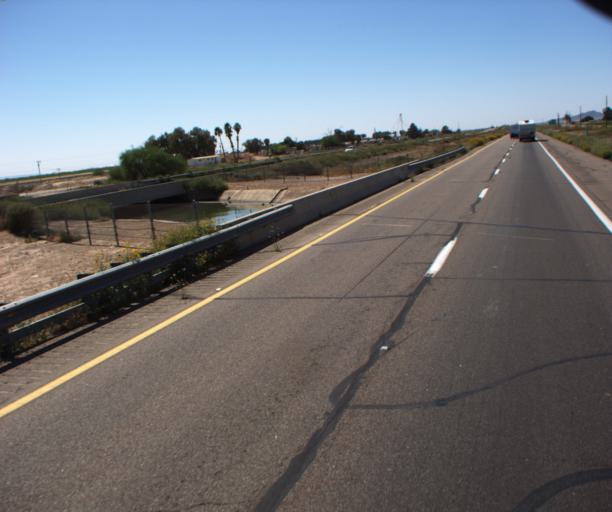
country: US
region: Arizona
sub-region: Maricopa County
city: Gila Bend
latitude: 32.9233
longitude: -112.8782
